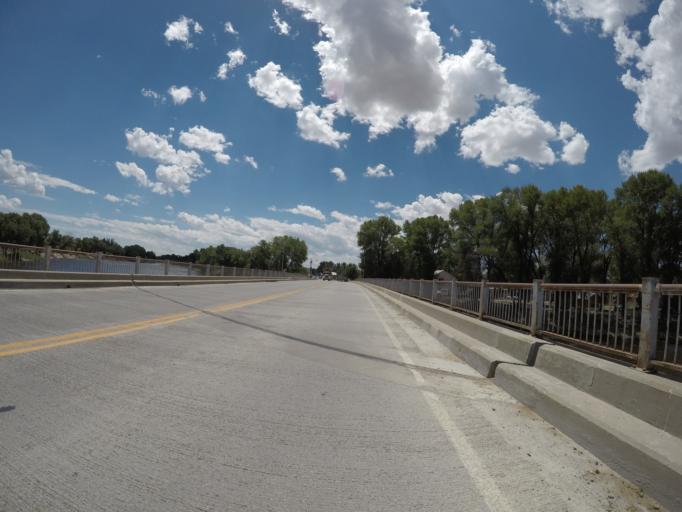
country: US
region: Wyoming
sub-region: Carbon County
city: Saratoga
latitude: 41.4591
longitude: -106.8075
